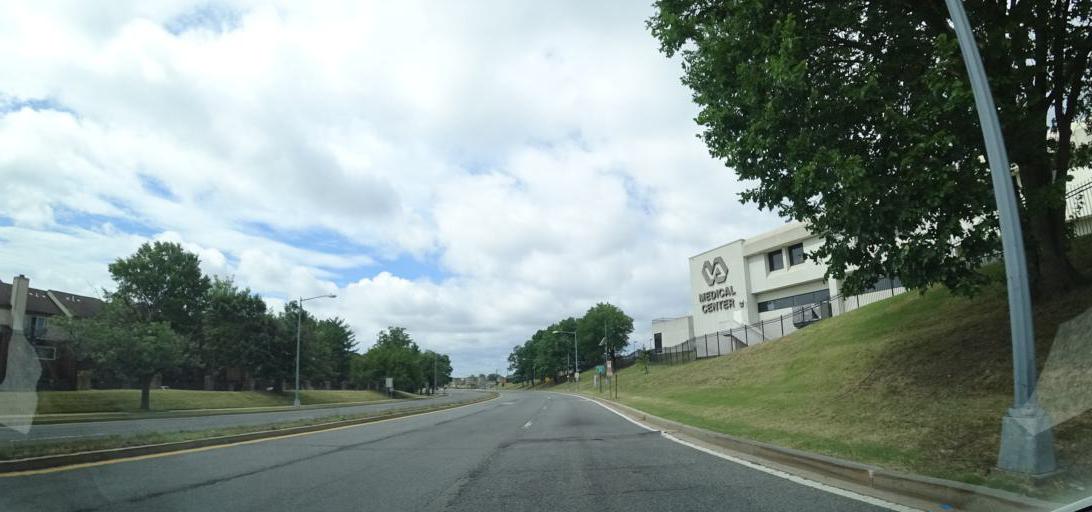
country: US
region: Maryland
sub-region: Prince George's County
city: Chillum
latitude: 38.9289
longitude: -77.0085
